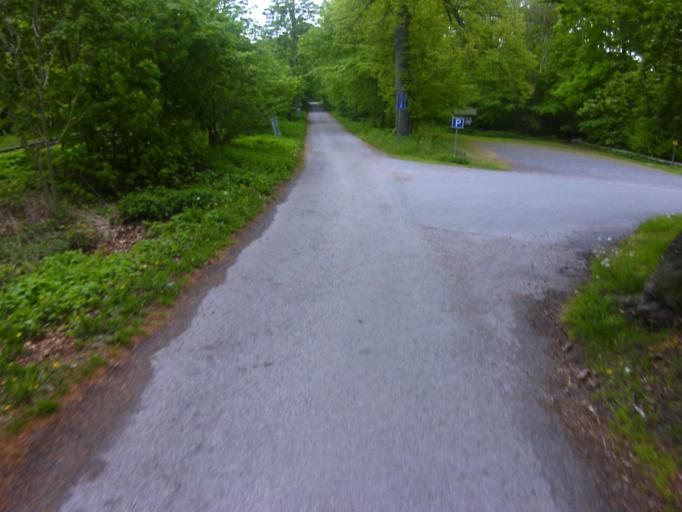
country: SE
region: Blekinge
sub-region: Solvesborgs Kommun
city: Soelvesborg
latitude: 56.0584
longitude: 14.5519
